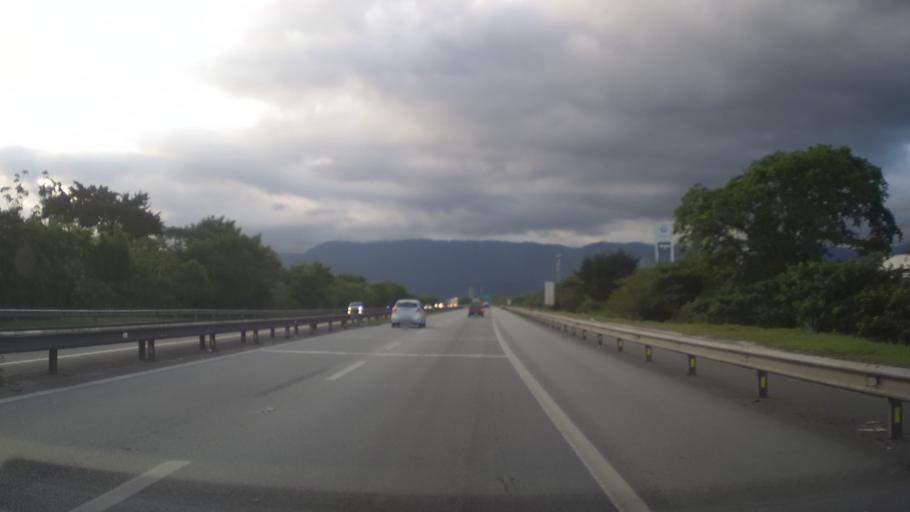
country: BR
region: Sao Paulo
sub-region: Sao Vicente
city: Sao Vicente
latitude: -23.9449
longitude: -46.4175
